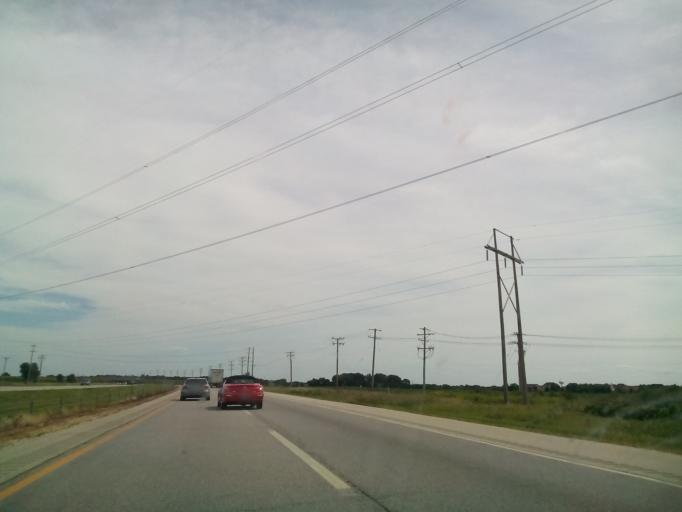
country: US
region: Illinois
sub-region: Kane County
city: Sugar Grove
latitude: 41.8062
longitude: -88.4371
